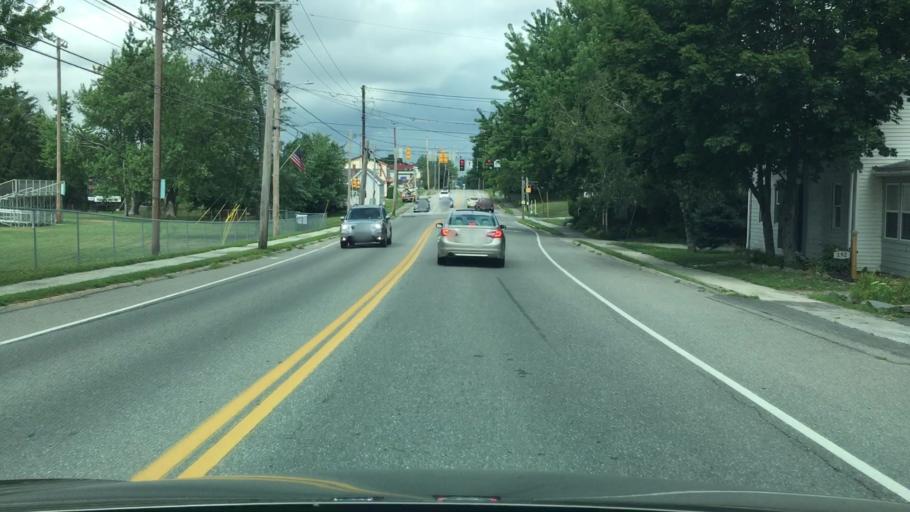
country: US
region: Maine
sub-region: Penobscot County
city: Brewer
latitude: 44.7890
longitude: -68.7554
